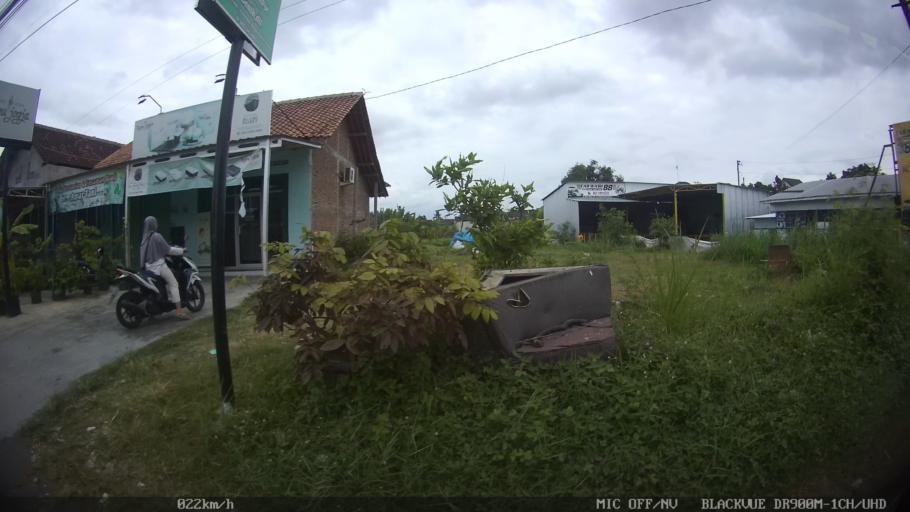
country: ID
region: Daerah Istimewa Yogyakarta
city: Sewon
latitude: -7.8369
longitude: 110.4118
